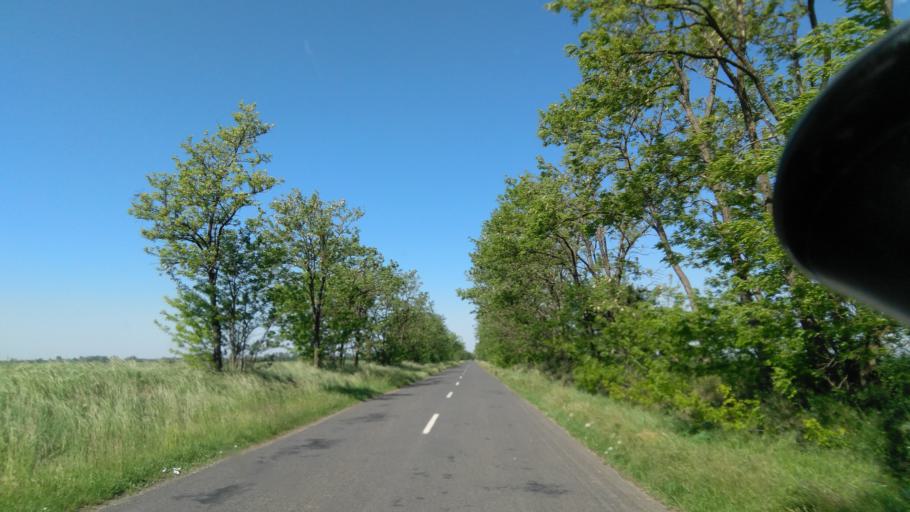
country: HU
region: Bekes
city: Kevermes
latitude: 46.4257
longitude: 21.1486
